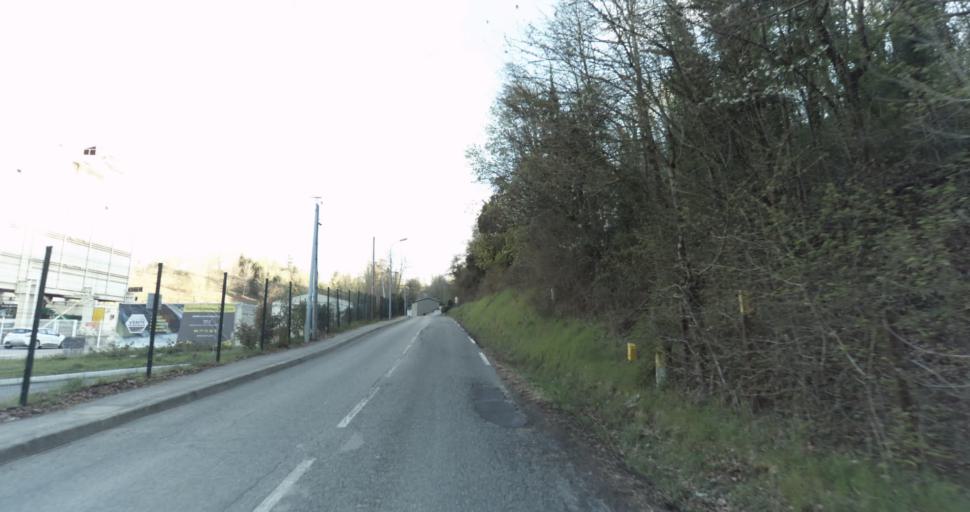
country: FR
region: Rhone-Alpes
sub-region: Departement de la Loire
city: La Talaudiere
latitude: 45.4666
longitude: 4.4394
